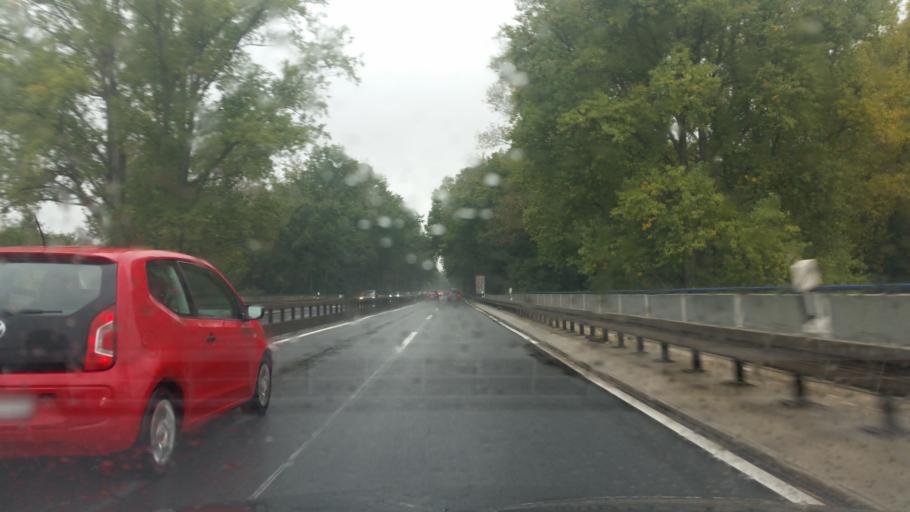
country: DE
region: Lower Saxony
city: Hemmingen
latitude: 52.3376
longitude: 9.7387
